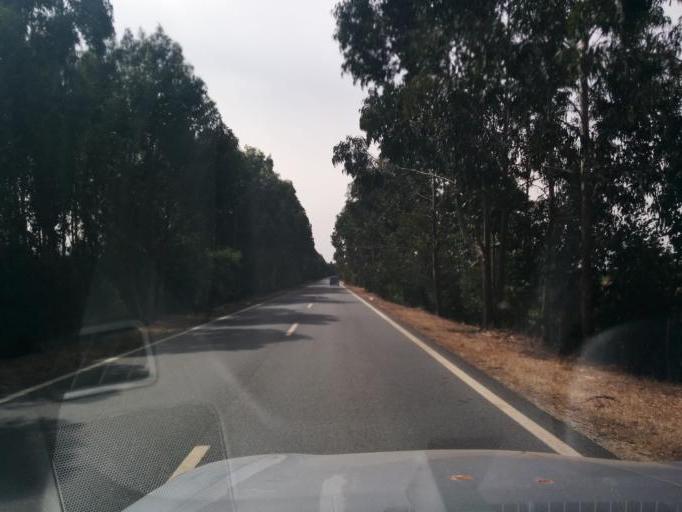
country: PT
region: Beja
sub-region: Odemira
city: Vila Nova de Milfontes
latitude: 37.6777
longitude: -8.7618
